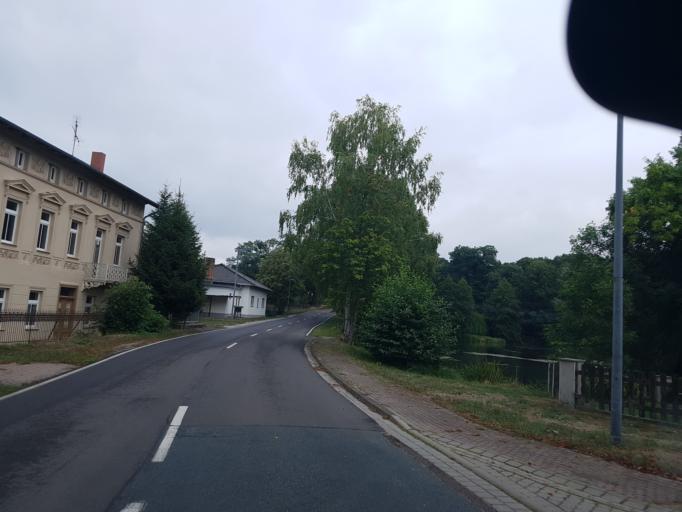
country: DE
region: Saxony-Anhalt
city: Tucheim
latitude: 52.2181
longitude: 12.1211
